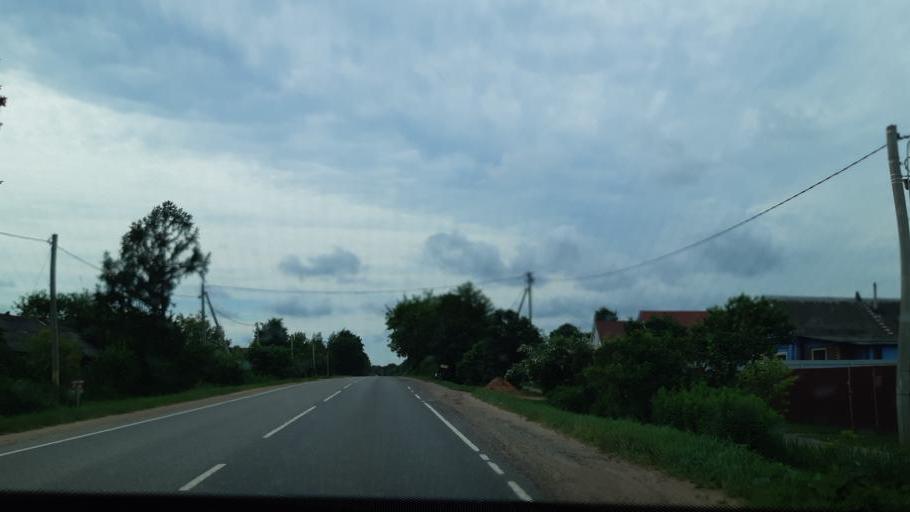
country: RU
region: Moskovskaya
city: Vereya
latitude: 55.3841
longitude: 36.3107
